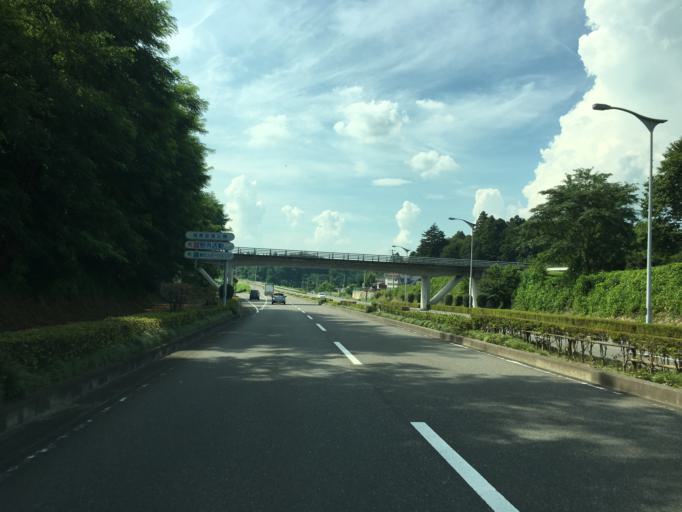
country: JP
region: Fukushima
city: Sukagawa
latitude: 37.2609
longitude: 140.4192
